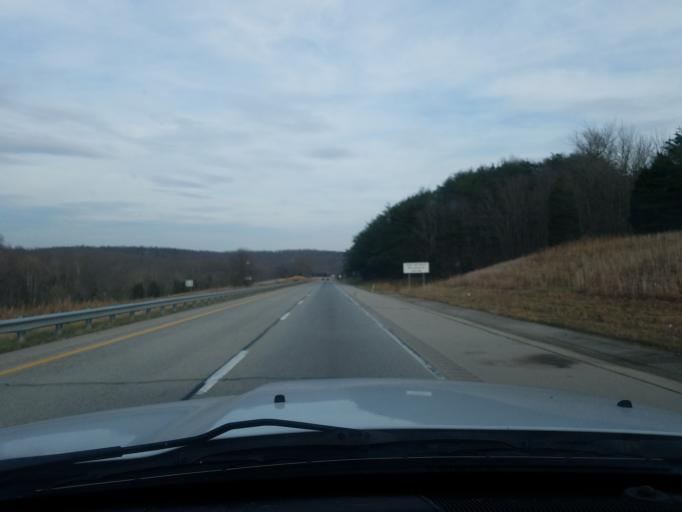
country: US
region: Indiana
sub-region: Crawford County
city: English
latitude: 38.2465
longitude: -86.3460
